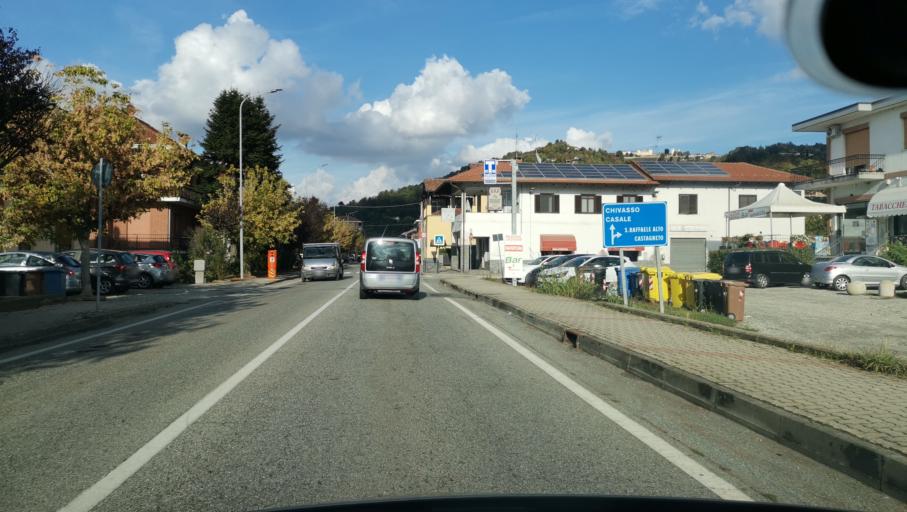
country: IT
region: Piedmont
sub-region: Provincia di Torino
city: San Raffaele Cimena
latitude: 45.1468
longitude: 7.8448
